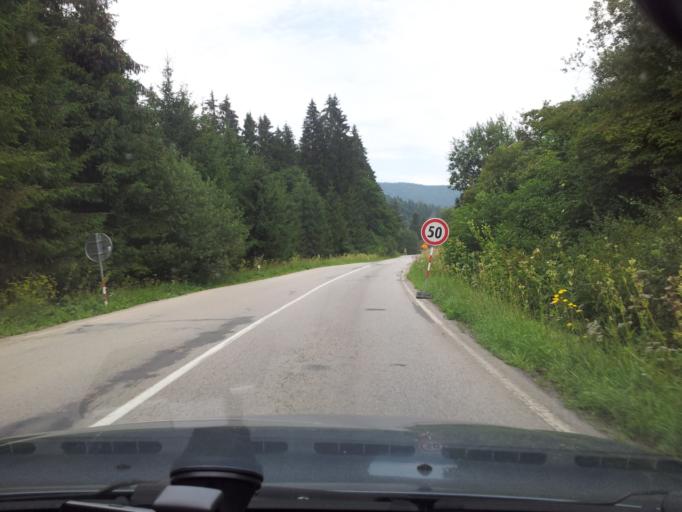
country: SK
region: Zilinsky
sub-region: Okres Dolny Kubin
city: Dolny Kubin
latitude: 49.2775
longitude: 19.3474
